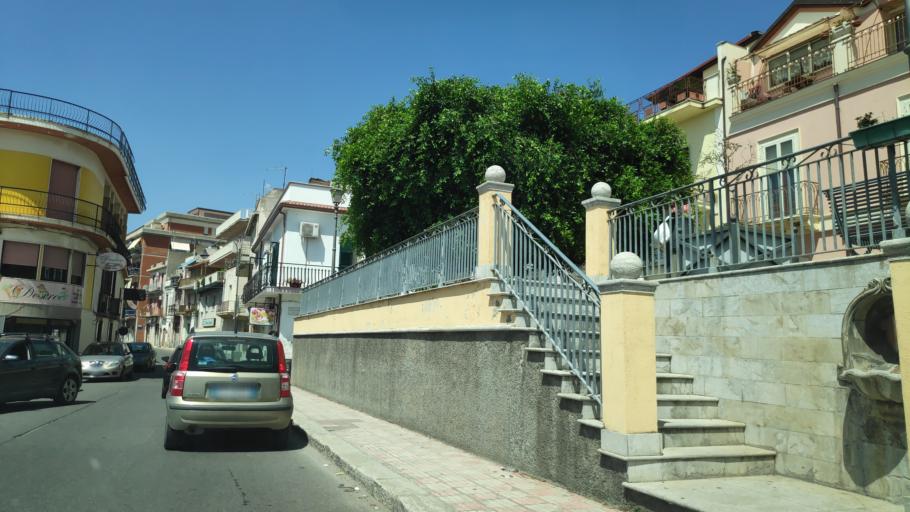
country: IT
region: Calabria
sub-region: Provincia di Reggio Calabria
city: Bova Marina
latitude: 37.9306
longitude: 15.9242
